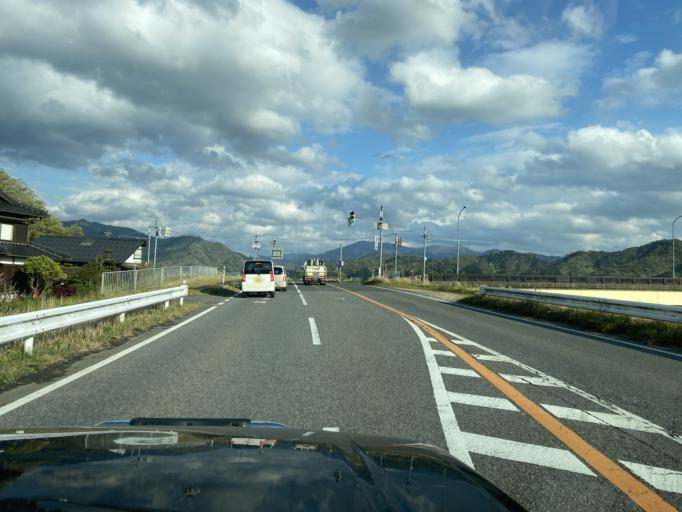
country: JP
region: Hyogo
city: Toyooka
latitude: 35.4930
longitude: 134.8413
